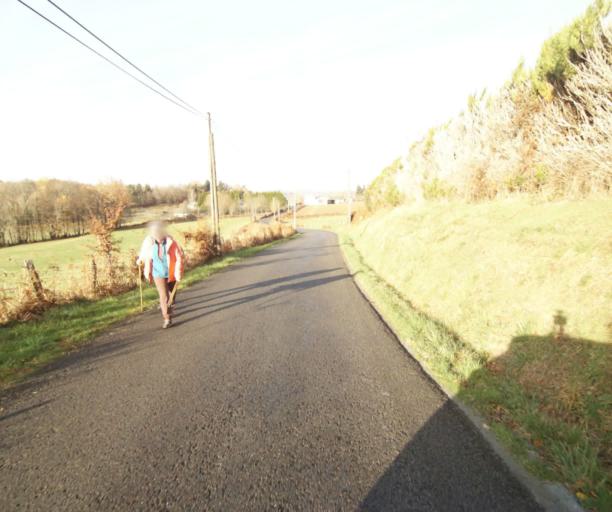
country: FR
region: Limousin
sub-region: Departement de la Correze
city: Cornil
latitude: 45.2069
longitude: 1.7095
